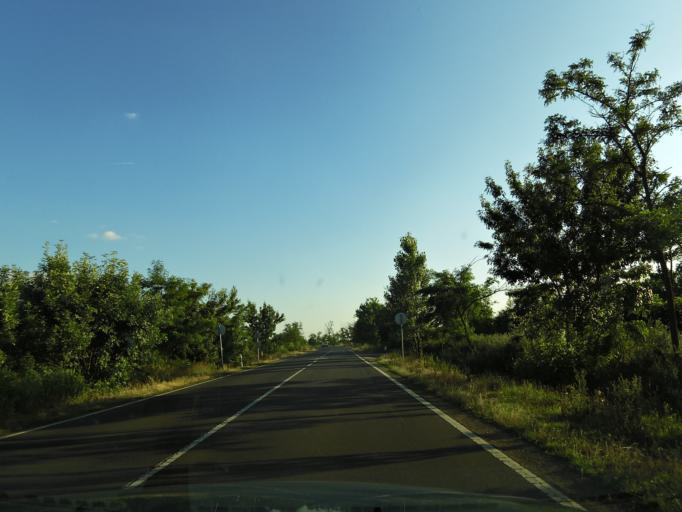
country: HU
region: Jasz-Nagykun-Szolnok
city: Kunszentmarton
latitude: 46.8798
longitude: 20.2678
